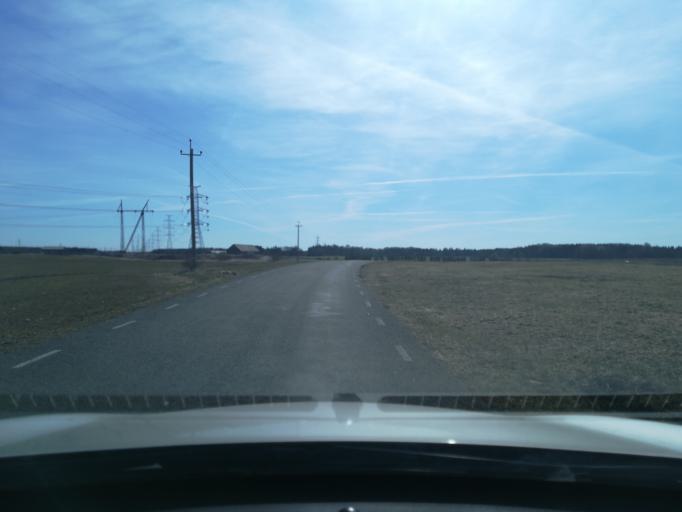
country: EE
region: Harju
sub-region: Saku vald
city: Saku
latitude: 59.2897
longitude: 24.6211
